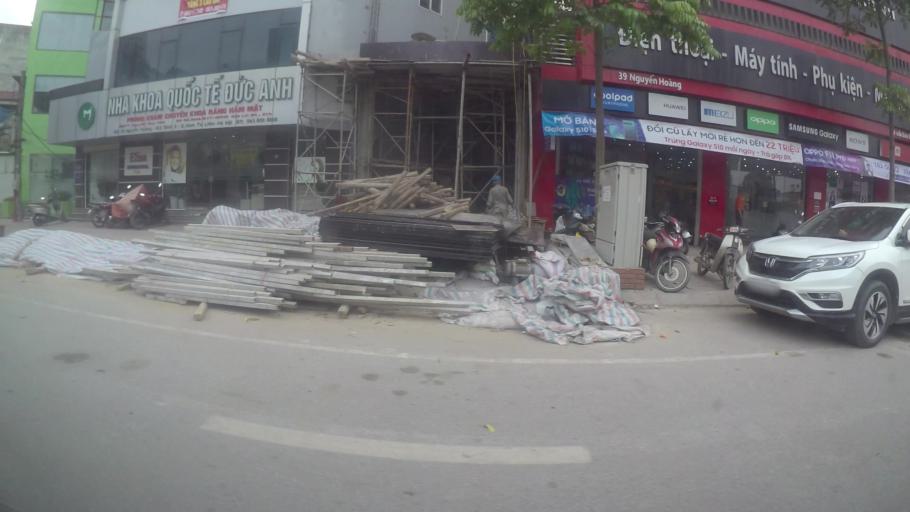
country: VN
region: Ha Noi
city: Cau Dien
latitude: 21.0317
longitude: 105.7740
